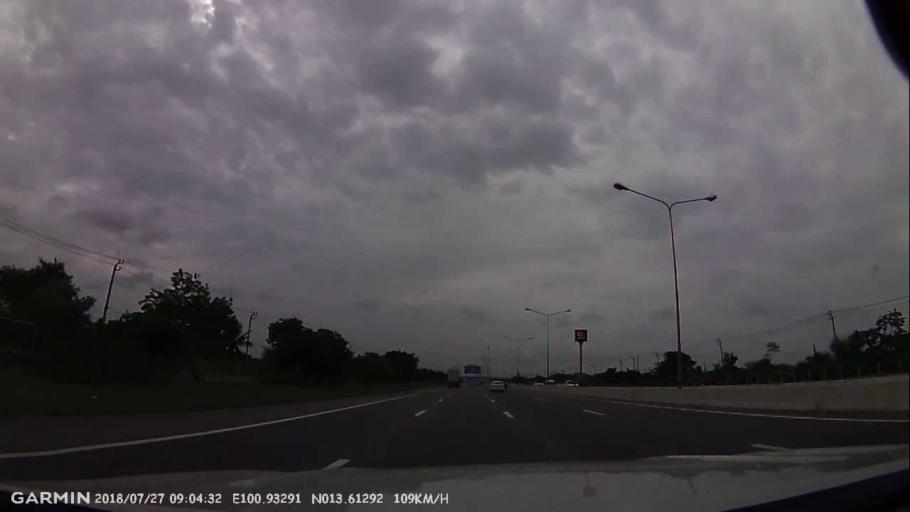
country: TH
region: Chachoengsao
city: Bang Pakong
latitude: 13.6125
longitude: 100.9336
